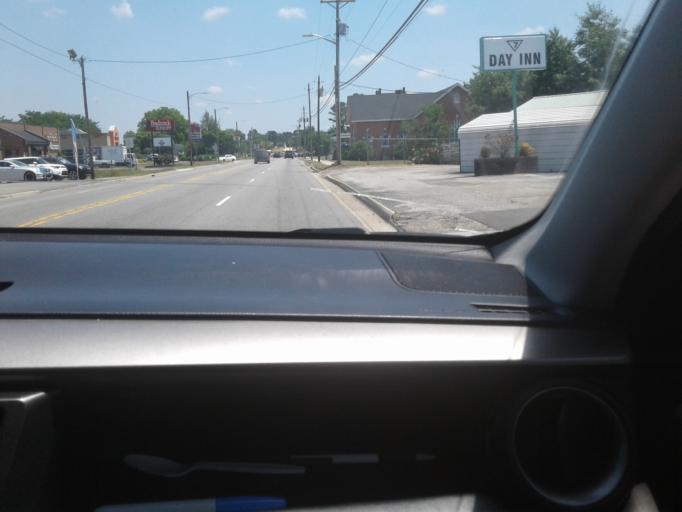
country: US
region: North Carolina
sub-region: Harnett County
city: Dunn
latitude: 35.3036
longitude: -78.6045
